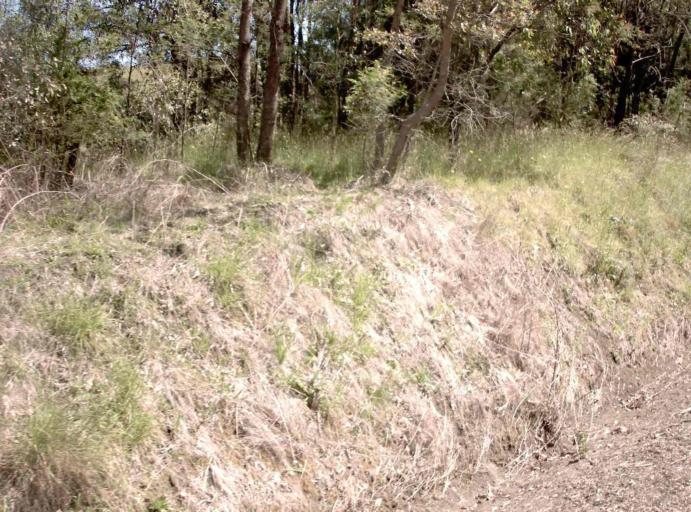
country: AU
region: Victoria
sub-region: East Gippsland
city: Lakes Entrance
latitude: -37.3563
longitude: 148.2281
